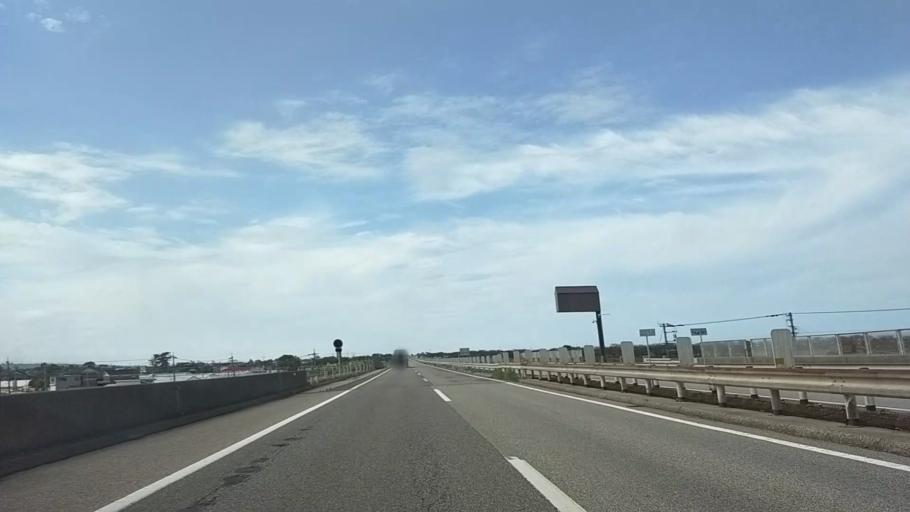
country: JP
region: Toyama
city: Nyuzen
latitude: 36.9378
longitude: 137.5461
